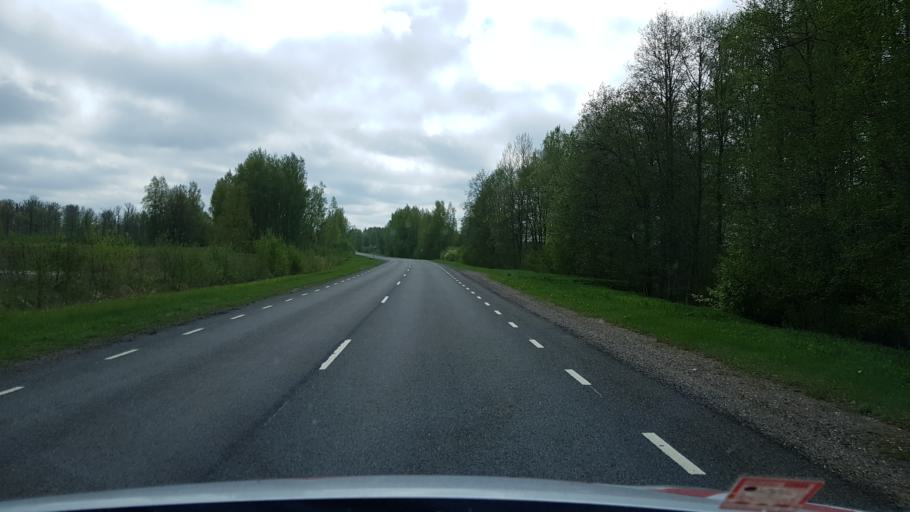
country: EE
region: Viljandimaa
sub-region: Karksi vald
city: Karksi-Nuia
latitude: 58.2057
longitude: 25.5367
